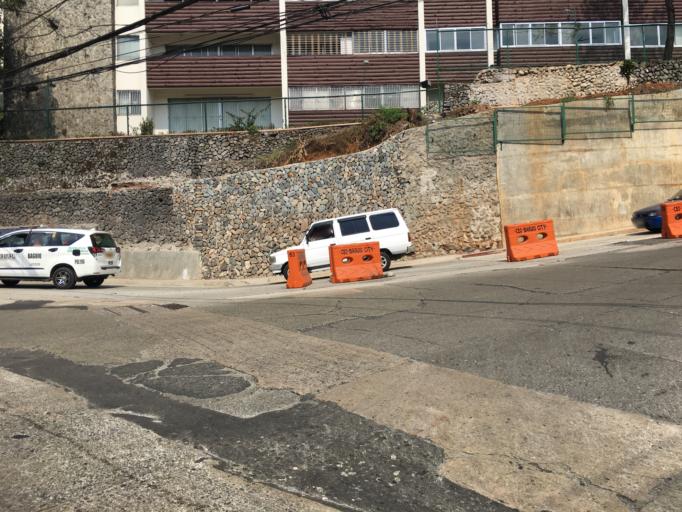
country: PH
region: Cordillera
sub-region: Baguio City
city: Baguio
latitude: 16.4015
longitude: 120.5937
